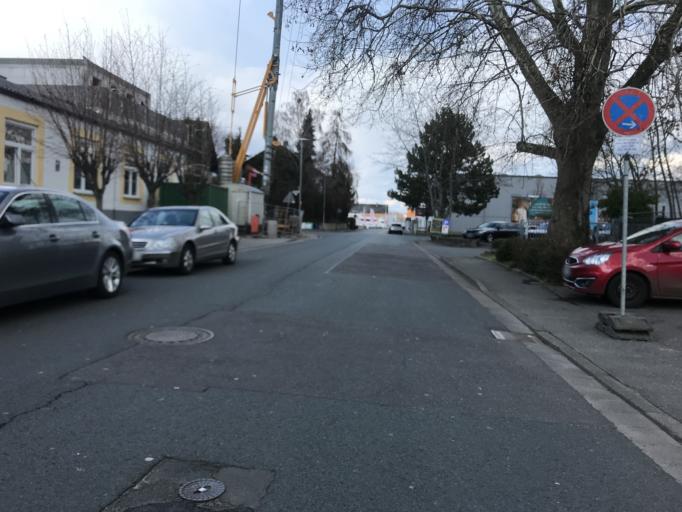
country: DE
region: Rheinland-Pfalz
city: Mainz
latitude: 49.9680
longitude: 8.2685
